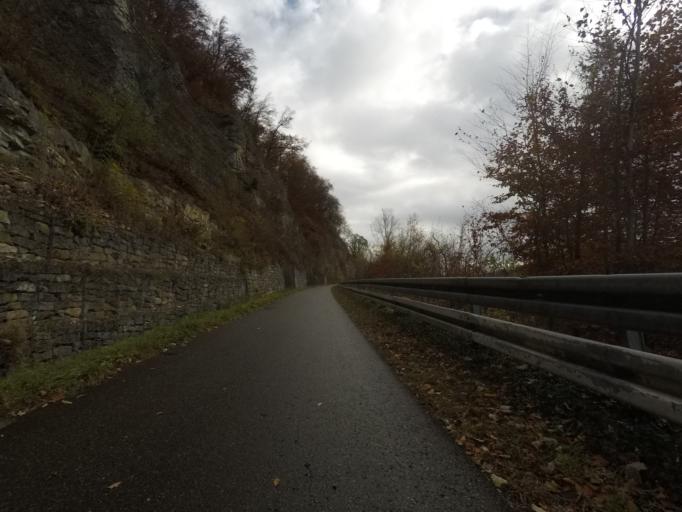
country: DE
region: Baden-Wuerttemberg
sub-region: Tuebingen Region
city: Pfullingen
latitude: 48.4077
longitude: 9.2689
